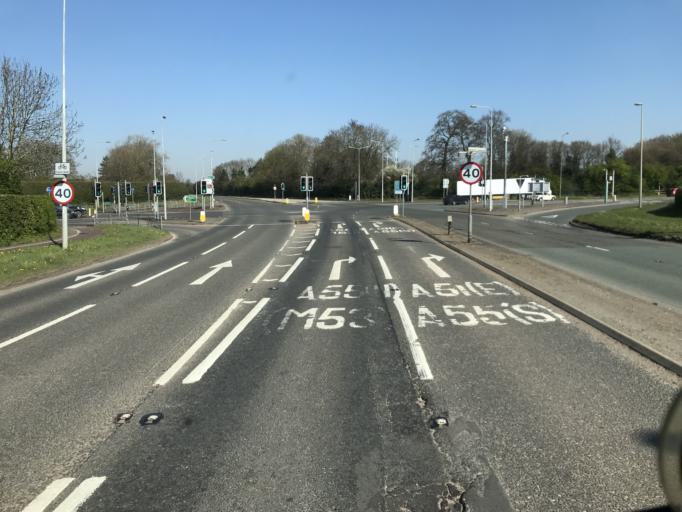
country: GB
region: England
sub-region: Cheshire West and Chester
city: Guilden Sutton
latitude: 53.1939
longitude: -2.8481
